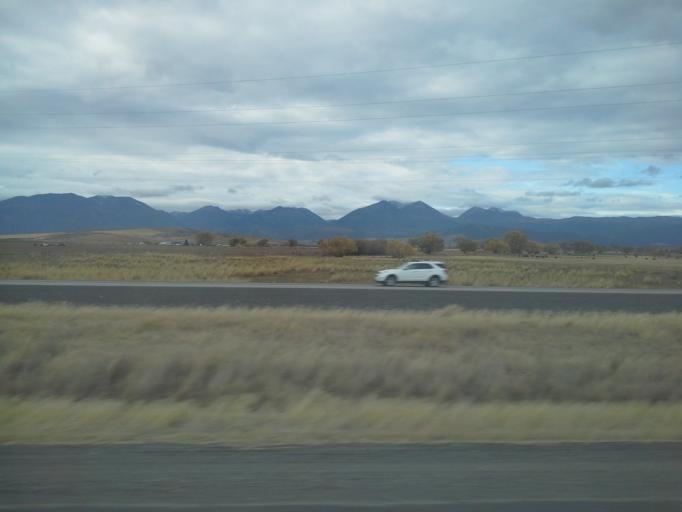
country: US
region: Oregon
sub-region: Union County
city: Union
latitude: 45.0078
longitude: -117.9113
